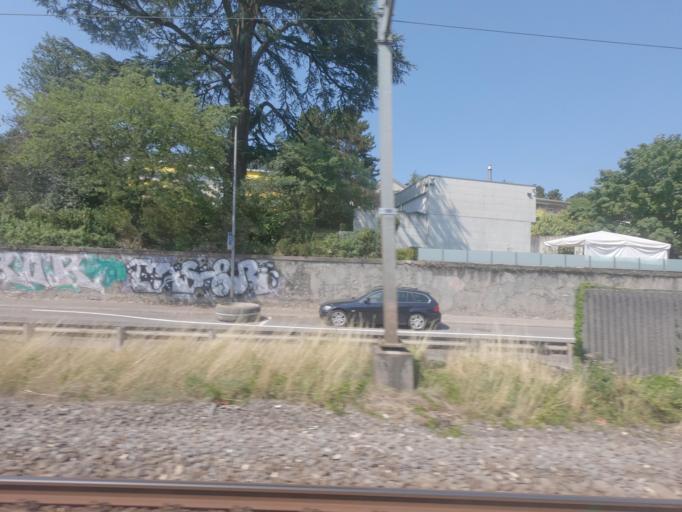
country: CH
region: Vaud
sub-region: Riviera-Pays-d'Enhaut District
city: Chardonne
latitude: 46.4690
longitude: 6.8315
